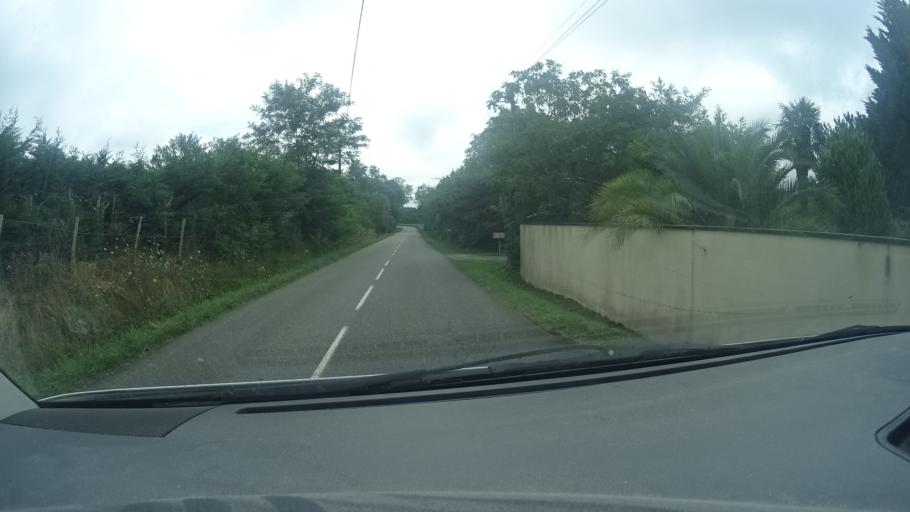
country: FR
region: Aquitaine
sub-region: Departement des Pyrenees-Atlantiques
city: Mont
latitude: 43.4896
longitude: -0.6772
